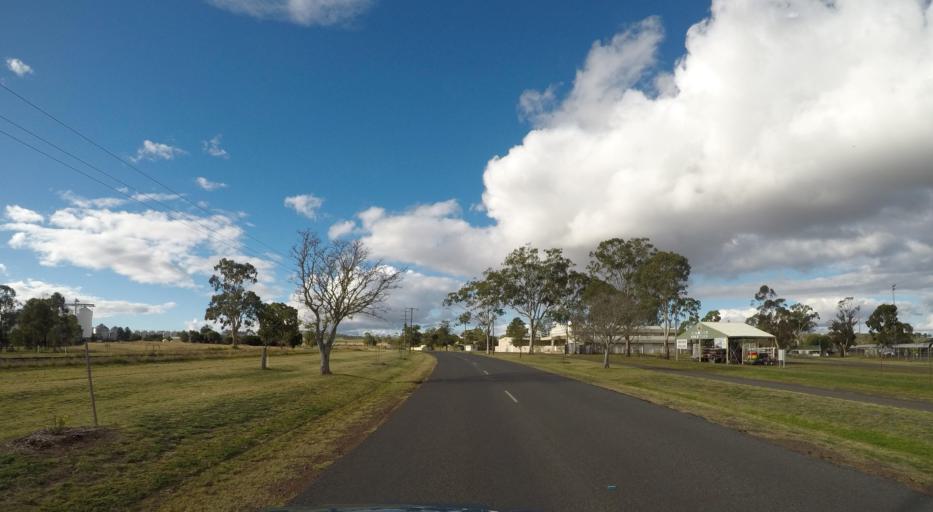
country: AU
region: Queensland
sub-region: Toowoomba
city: Westbrook
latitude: -27.7122
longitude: 151.6404
